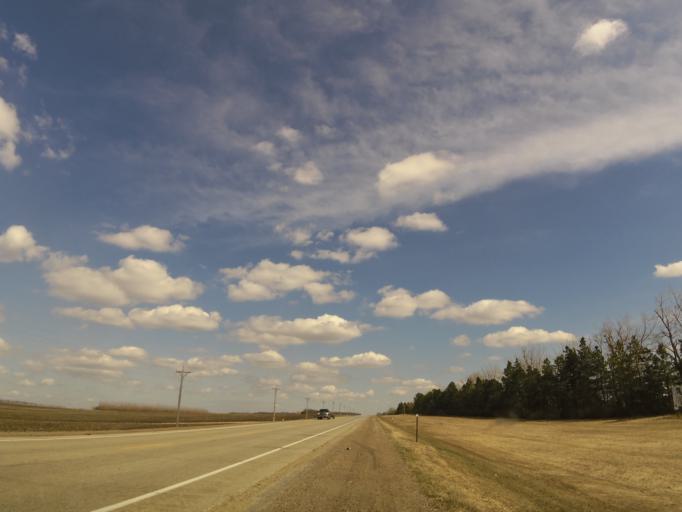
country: US
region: South Dakota
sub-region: Codington County
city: Watertown
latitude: 44.8900
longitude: -96.9540
